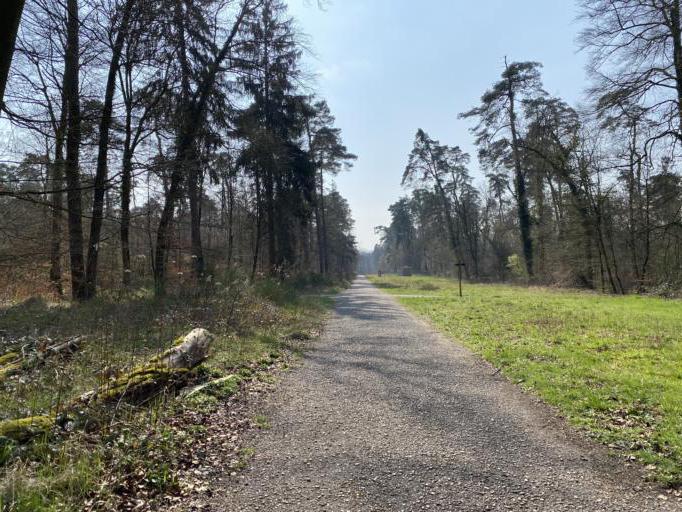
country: DE
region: Baden-Wuerttemberg
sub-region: Karlsruhe Region
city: Karlsruhe
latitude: 49.0477
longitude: 8.4165
